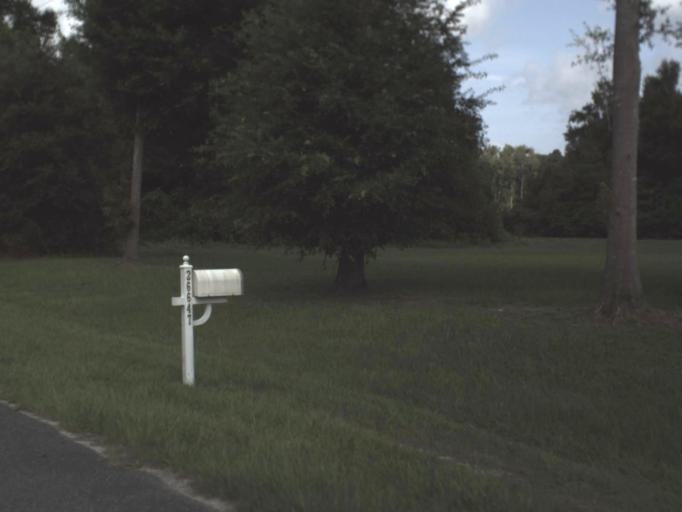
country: US
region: Florida
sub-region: Lafayette County
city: Mayo
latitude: 29.9653
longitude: -82.9110
